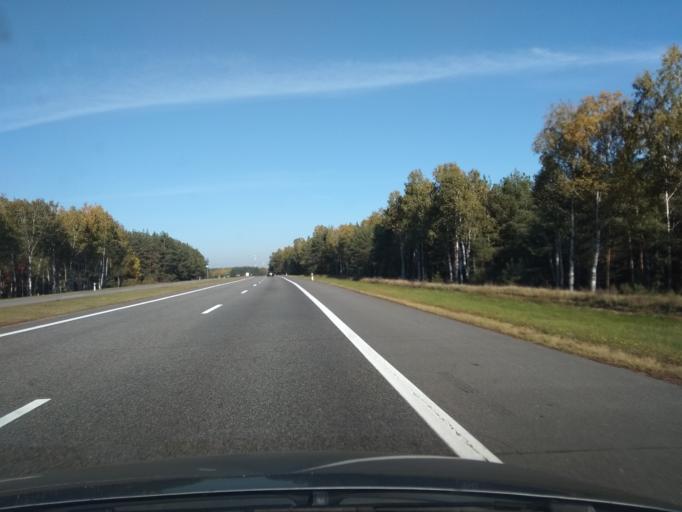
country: BY
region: Brest
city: Baranovichi
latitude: 53.0712
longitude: 25.8807
